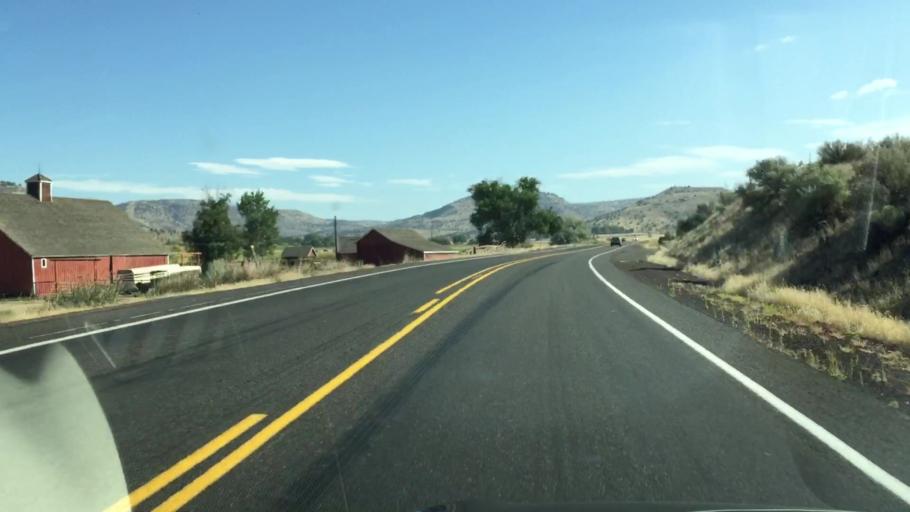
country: US
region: Oregon
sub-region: Jefferson County
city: Madras
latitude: 44.7947
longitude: -120.9489
